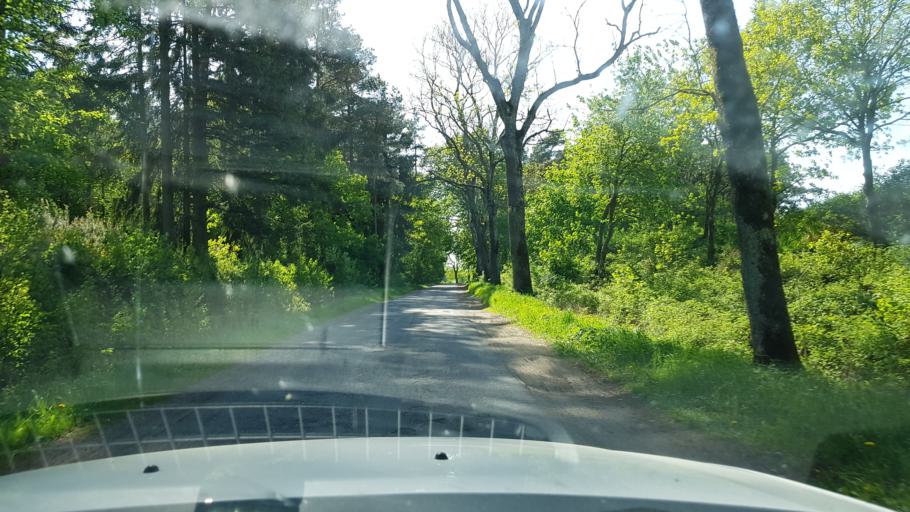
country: PL
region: West Pomeranian Voivodeship
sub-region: Powiat kolobrzeski
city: Ryman
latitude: 53.9936
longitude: 15.5271
